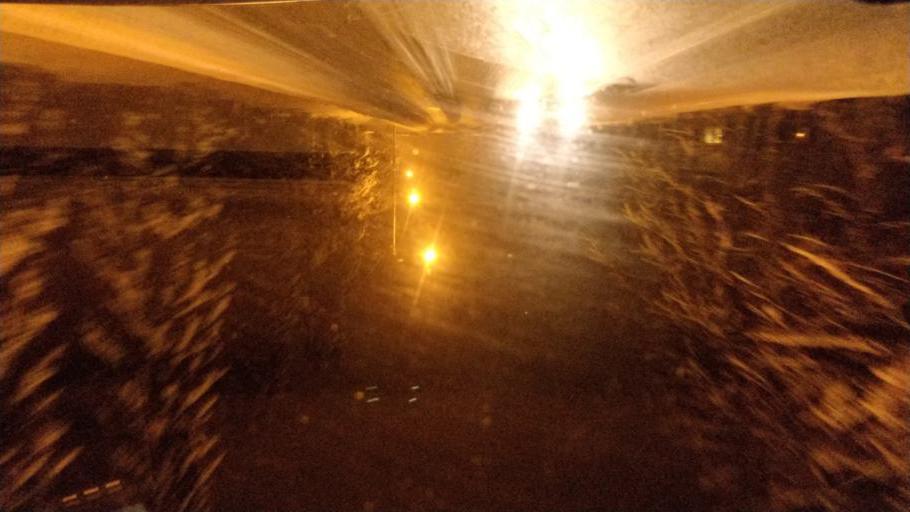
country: FI
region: Lapland
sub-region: Rovaniemi
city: Rovaniemi
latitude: 66.4157
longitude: 25.4123
